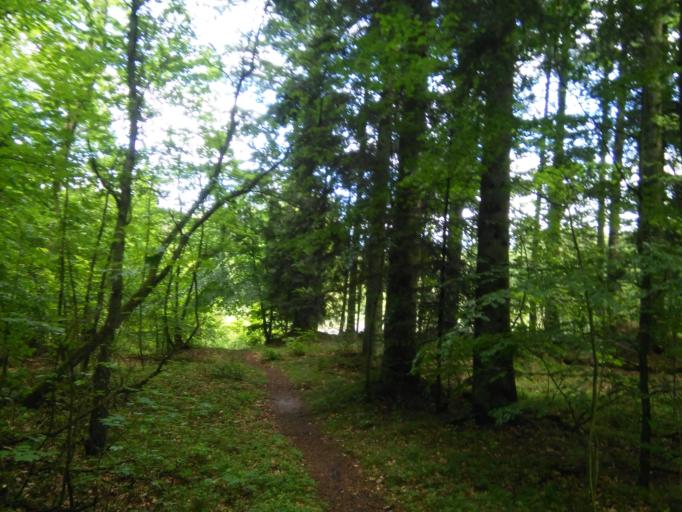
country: DK
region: Capital Region
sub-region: Bornholm Kommune
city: Nexo
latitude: 55.0939
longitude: 15.1052
